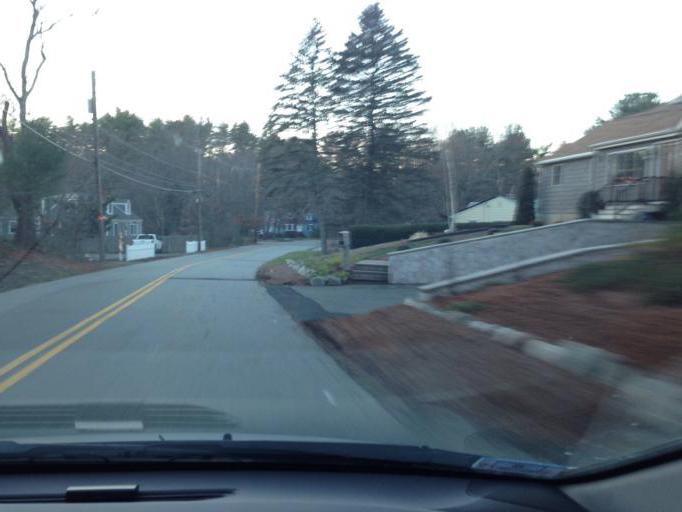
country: US
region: Massachusetts
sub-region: Middlesex County
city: Bedford
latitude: 42.4956
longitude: -71.2689
